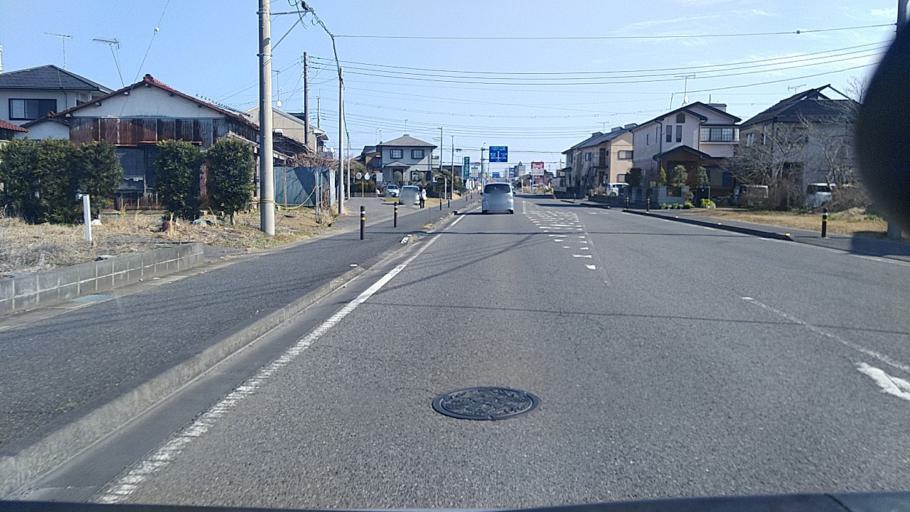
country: JP
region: Chiba
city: Mobara
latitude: 35.4250
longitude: 140.2832
